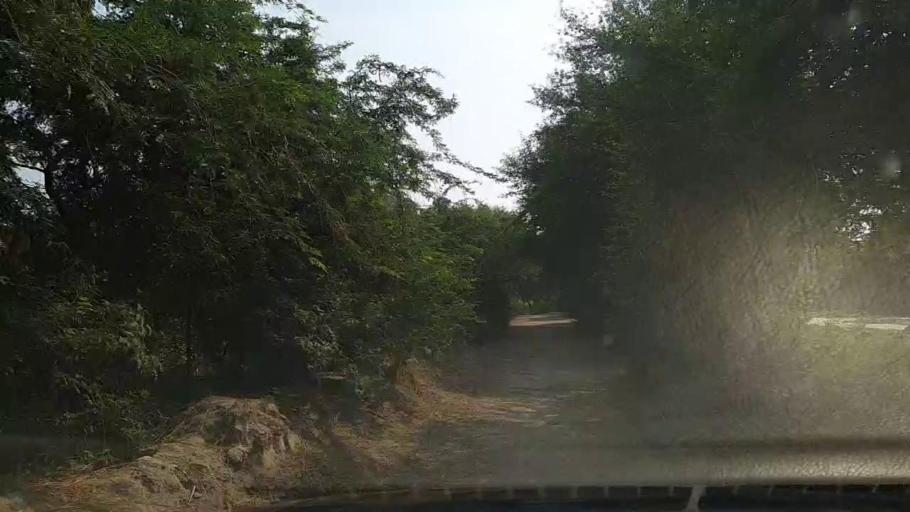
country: PK
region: Sindh
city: Mirpur Batoro
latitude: 24.6911
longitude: 68.2209
